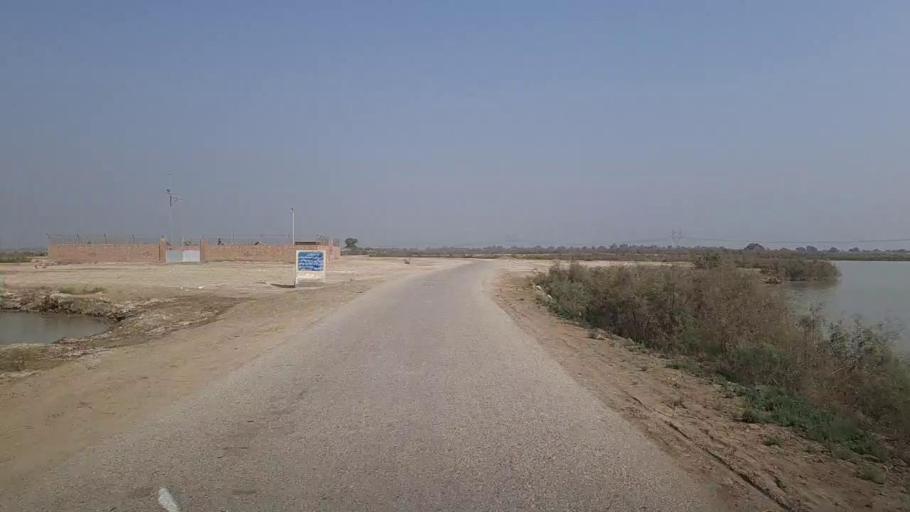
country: PK
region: Sindh
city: Kandhkot
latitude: 28.2260
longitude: 69.2018
